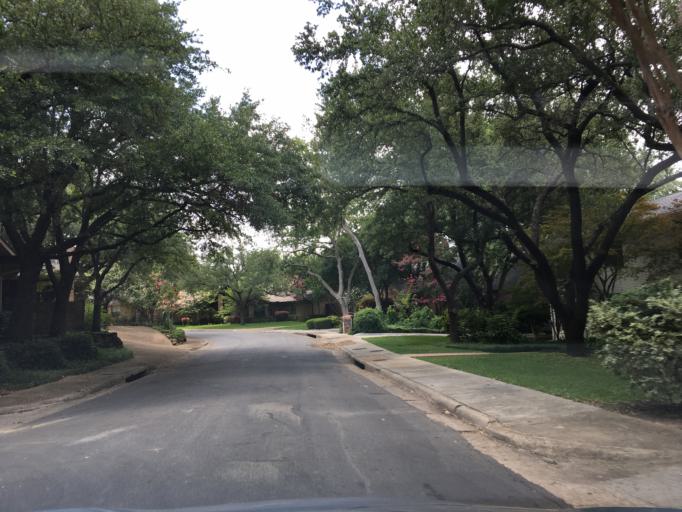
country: US
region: Texas
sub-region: Dallas County
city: University Park
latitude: 32.8933
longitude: -96.7846
